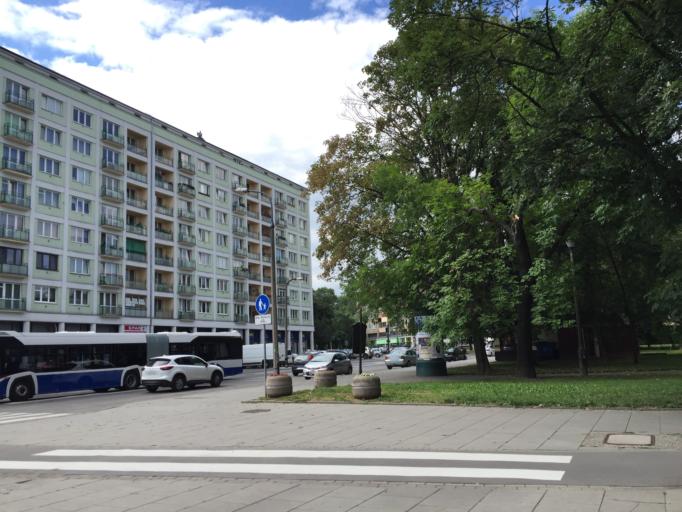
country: PL
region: Lesser Poland Voivodeship
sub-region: Powiat wielicki
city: Kokotow
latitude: 50.0737
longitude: 20.0427
